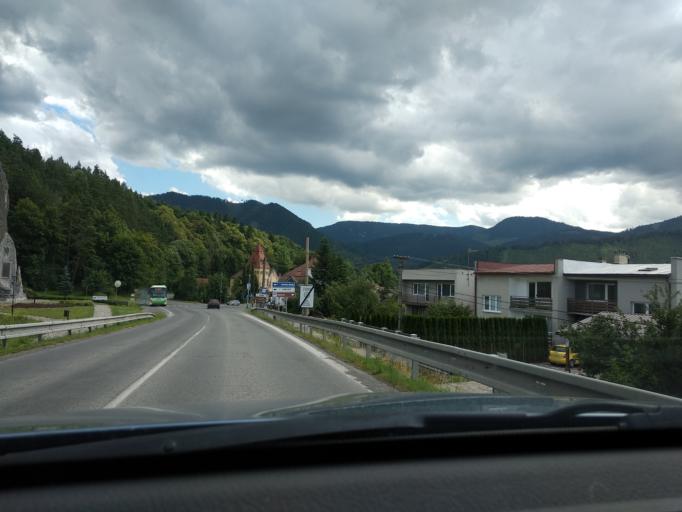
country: SK
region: Zilinsky
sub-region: Okres Zilina
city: Liptovsky Hradok
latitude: 49.0454
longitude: 19.7313
